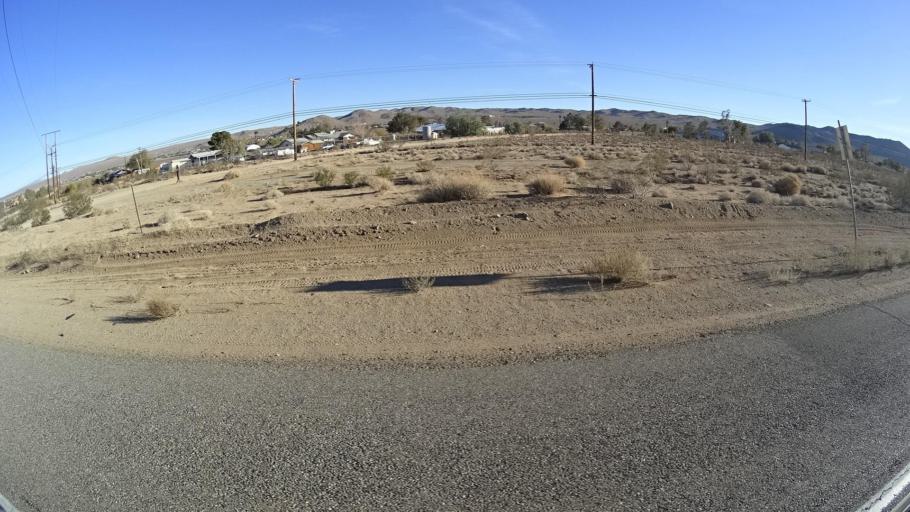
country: US
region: California
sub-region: Kern County
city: Ridgecrest
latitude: 35.5933
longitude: -117.6916
